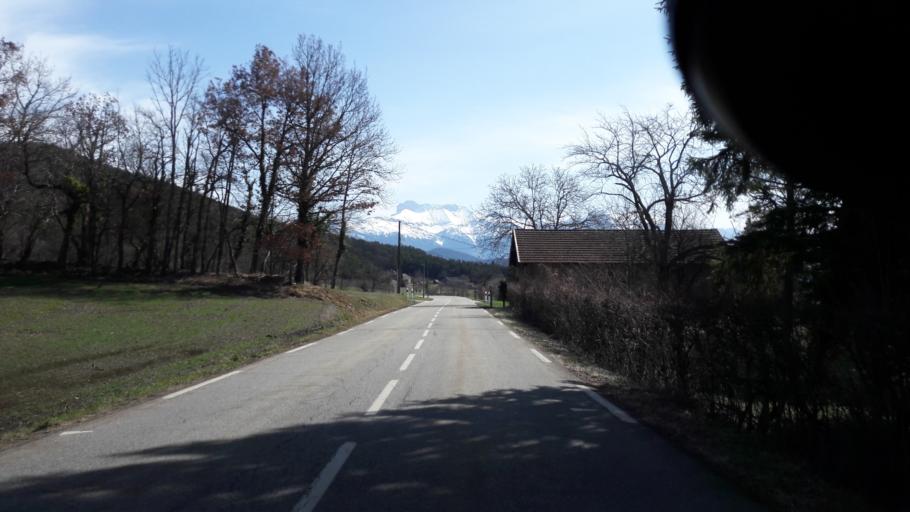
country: FR
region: Rhone-Alpes
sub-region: Departement de l'Isere
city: La Motte-Saint-Martin
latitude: 44.8857
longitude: 5.6416
